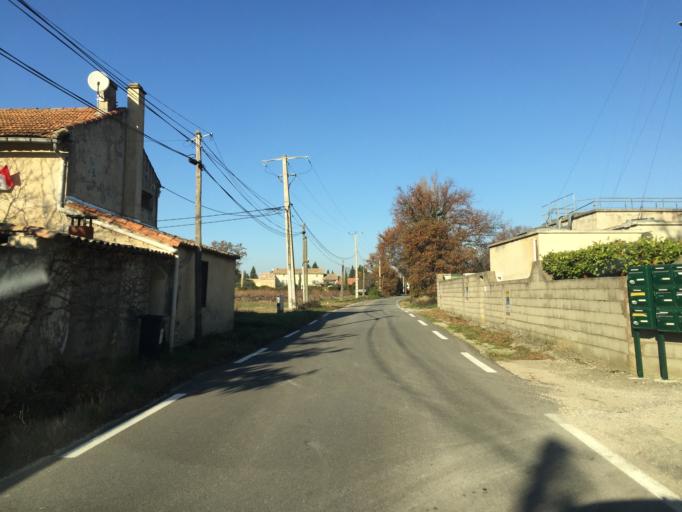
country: FR
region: Provence-Alpes-Cote d'Azur
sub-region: Departement du Vaucluse
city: Camaret-sur-Aigues
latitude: 44.1712
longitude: 4.8787
